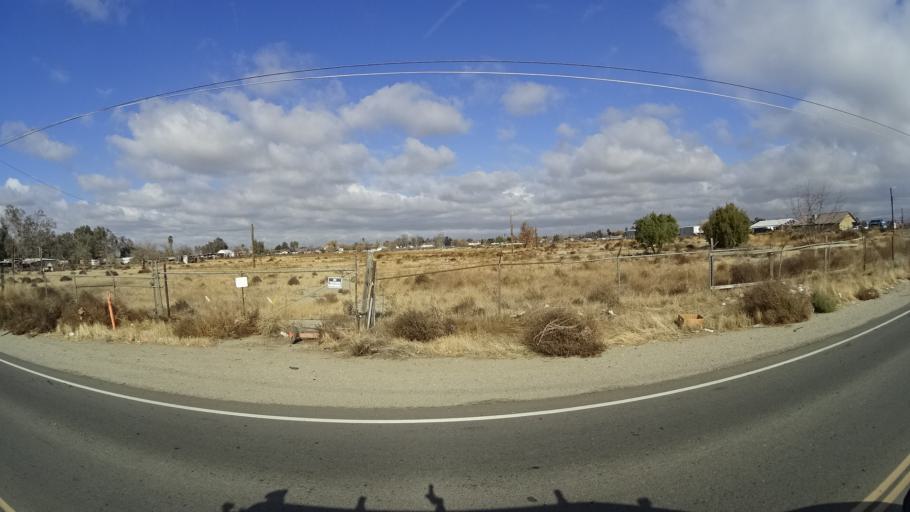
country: US
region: California
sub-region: Kern County
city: Greenfield
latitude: 35.3177
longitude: -118.9889
